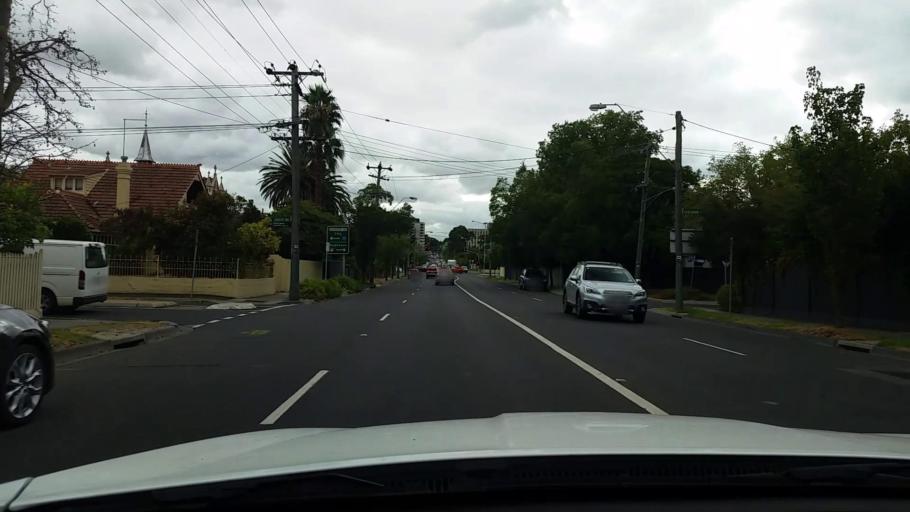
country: AU
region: Victoria
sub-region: Boroondara
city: Kew
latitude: -37.8153
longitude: 145.0276
